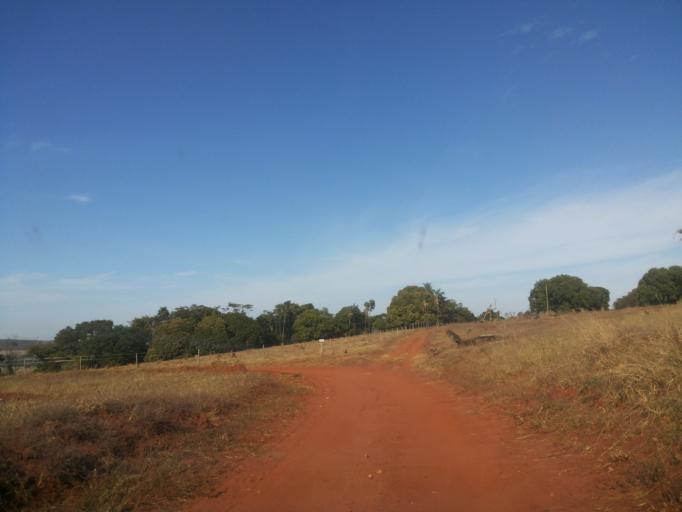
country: BR
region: Minas Gerais
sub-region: Ituiutaba
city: Ituiutaba
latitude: -19.1099
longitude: -49.4173
